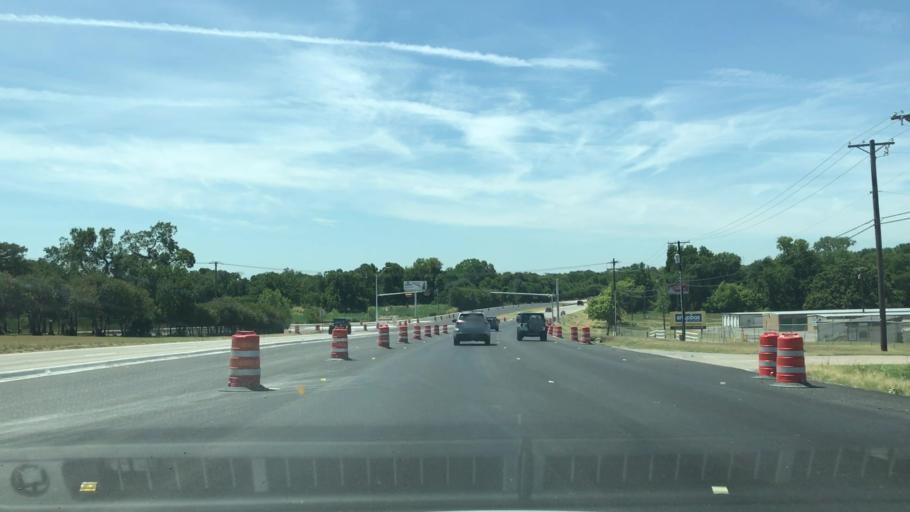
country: US
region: Texas
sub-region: Collin County
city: McKinney
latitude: 33.1775
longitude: -96.6195
